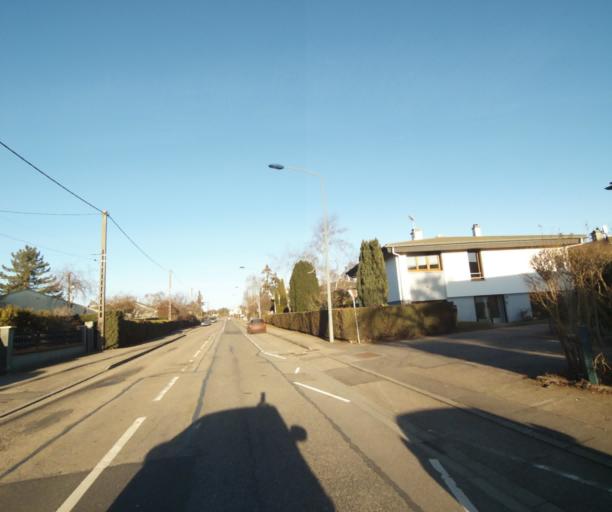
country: FR
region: Lorraine
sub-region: Departement de Meurthe-et-Moselle
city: Seichamps
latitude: 48.7117
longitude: 6.2561
